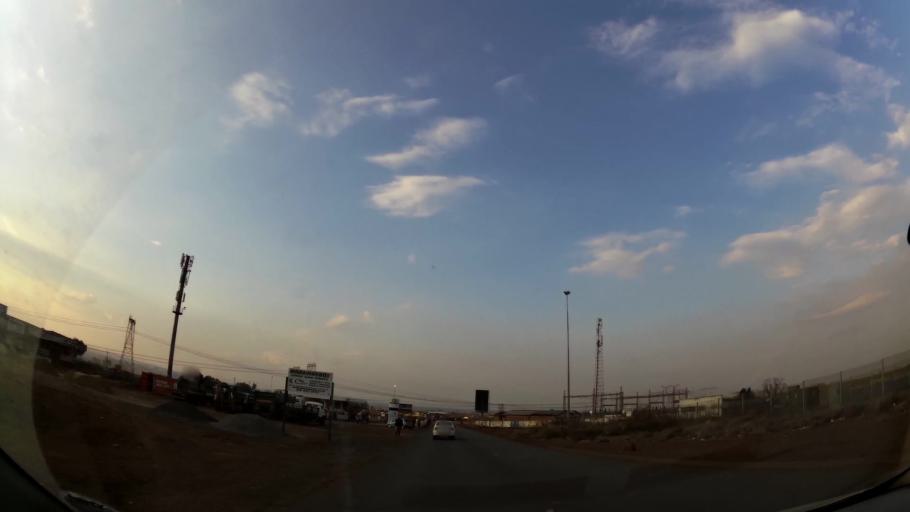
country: ZA
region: Gauteng
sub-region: City of Johannesburg Metropolitan Municipality
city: Orange Farm
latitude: -26.5595
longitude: 27.8614
